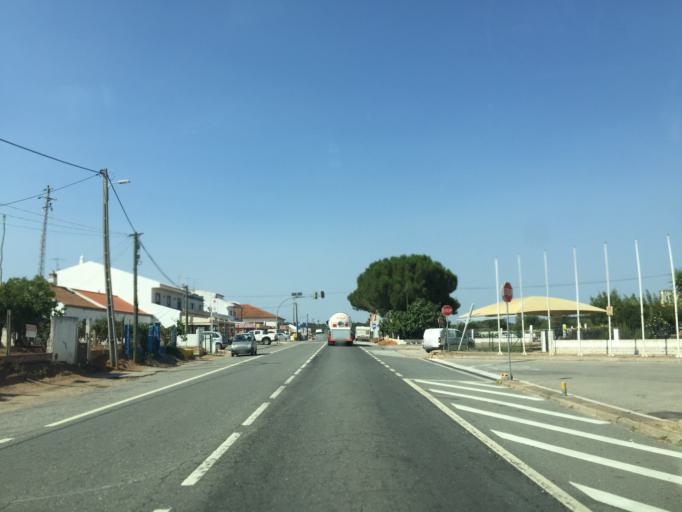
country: PT
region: Beja
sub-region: Aljustrel
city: Aljustrel
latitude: 37.9463
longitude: -8.3806
